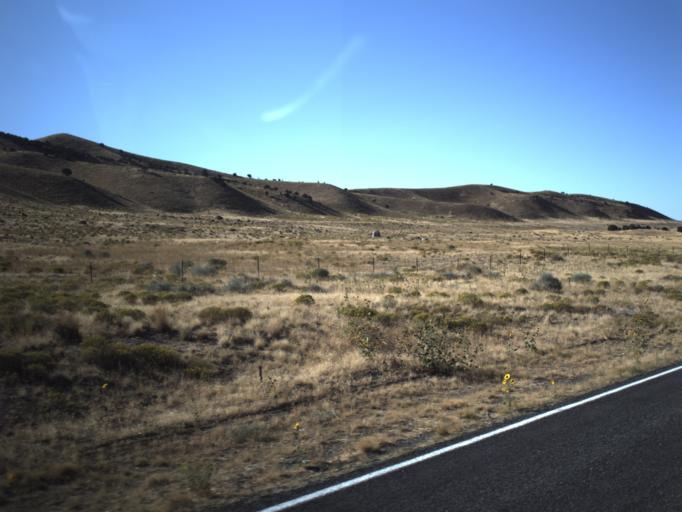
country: US
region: Utah
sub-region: Millard County
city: Delta
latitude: 39.4485
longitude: -112.3087
